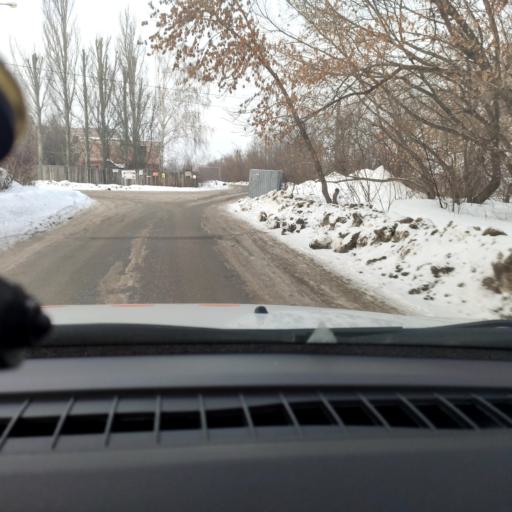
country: RU
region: Samara
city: Samara
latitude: 53.1342
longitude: 50.1359
